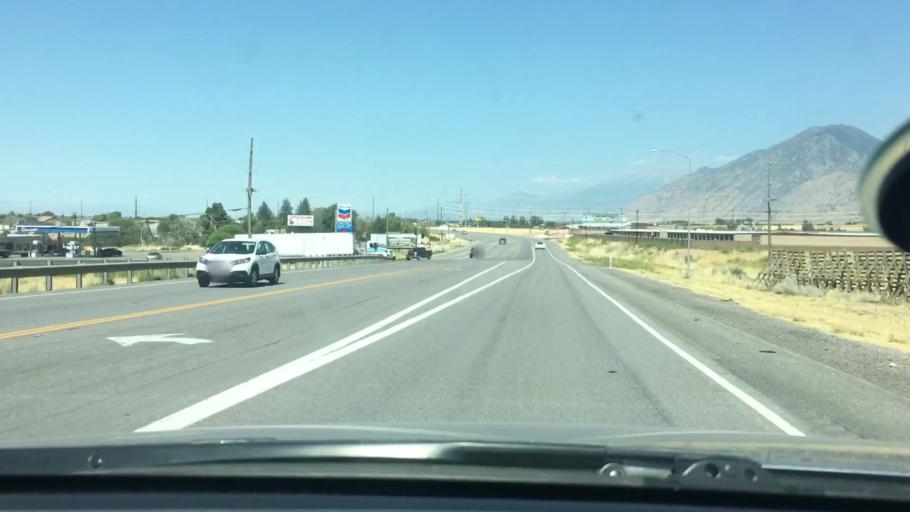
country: US
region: Utah
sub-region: Utah County
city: Mapleton
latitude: 40.0849
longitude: -111.5928
